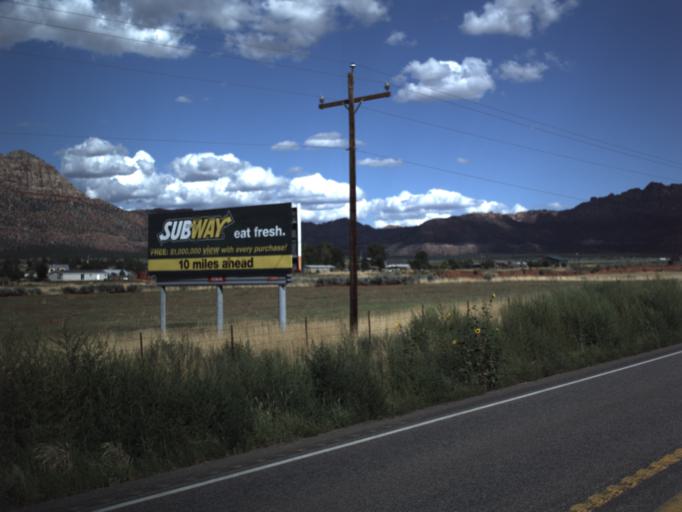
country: US
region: Utah
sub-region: Washington County
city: LaVerkin
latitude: 37.0989
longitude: -113.1266
